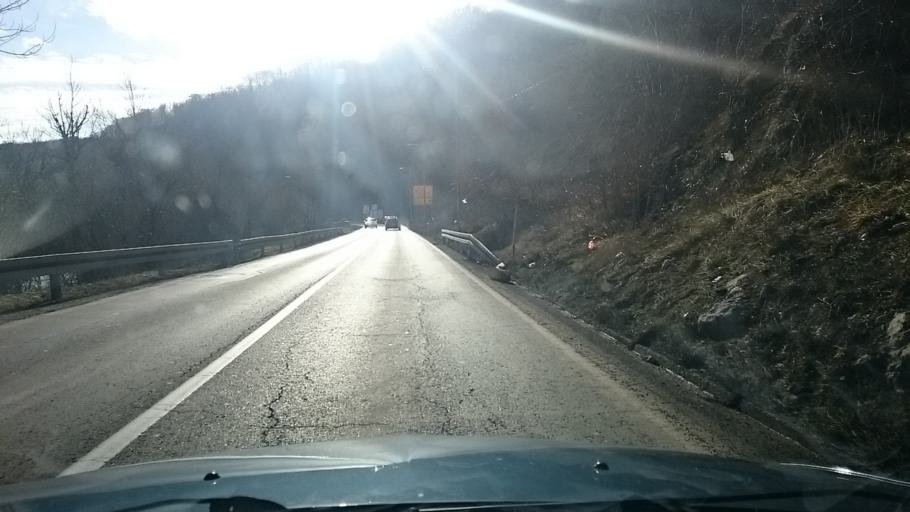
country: BA
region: Republika Srpska
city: Hiseti
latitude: 44.7446
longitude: 17.1540
